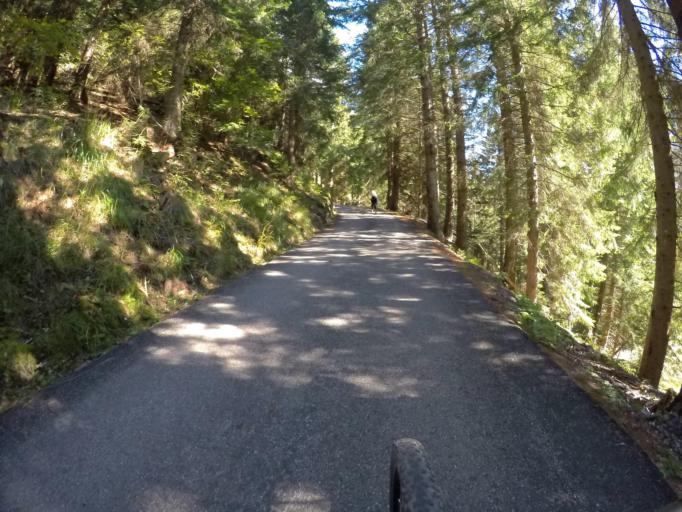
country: IT
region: Friuli Venezia Giulia
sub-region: Provincia di Udine
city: Ligosullo
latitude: 46.5492
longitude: 13.0922
